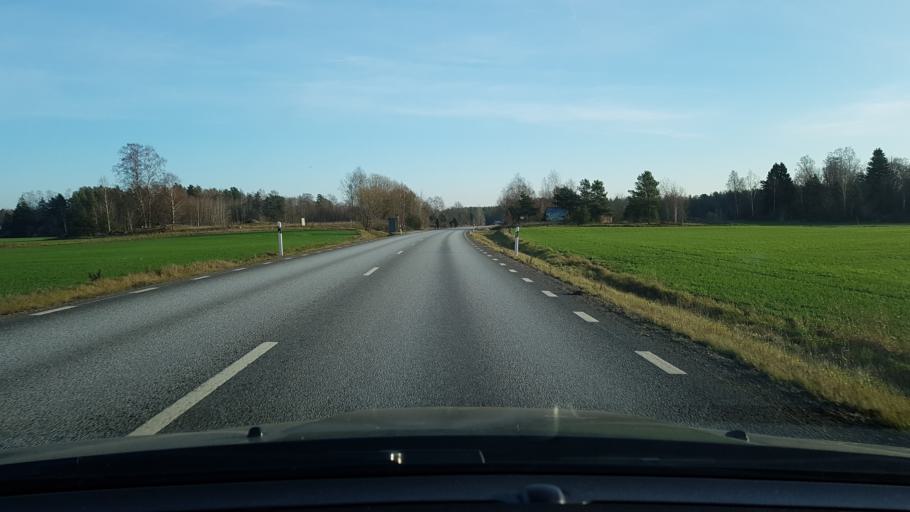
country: SE
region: Stockholm
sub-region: Vallentuna Kommun
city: Vallentuna
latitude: 59.7490
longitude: 18.0666
